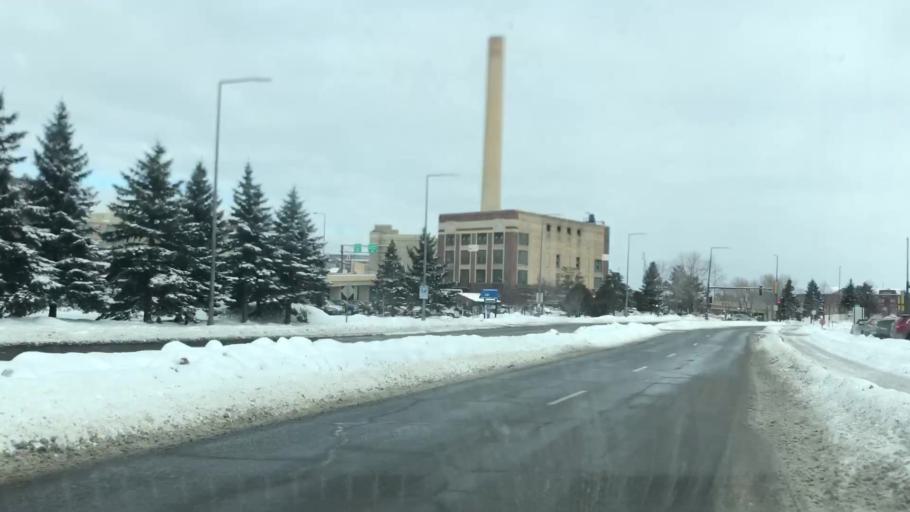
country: US
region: Minnesota
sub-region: Saint Louis County
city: Duluth
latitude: 46.7837
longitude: -92.0983
